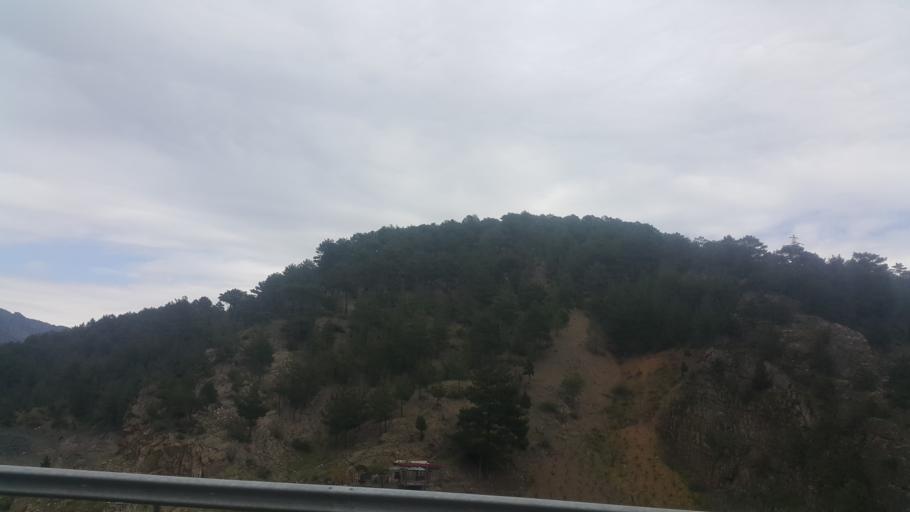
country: TR
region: Nigde
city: Ciftehan
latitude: 37.5176
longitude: 34.8177
